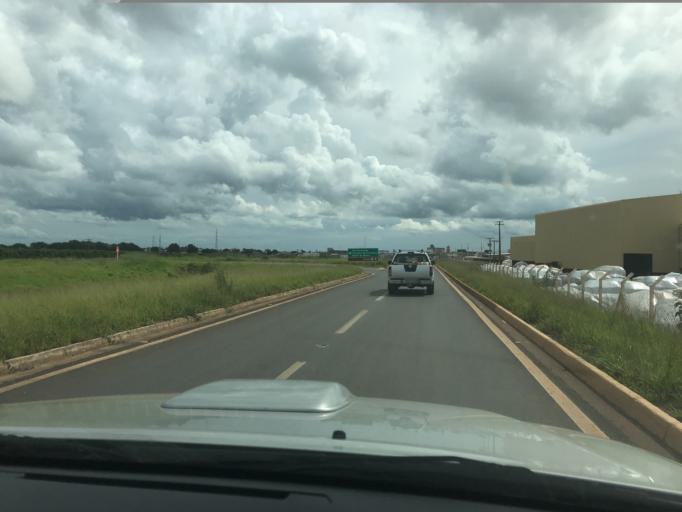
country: BR
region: Minas Gerais
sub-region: Patrocinio
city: Patrocinio
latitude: -19.0968
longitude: -46.6728
